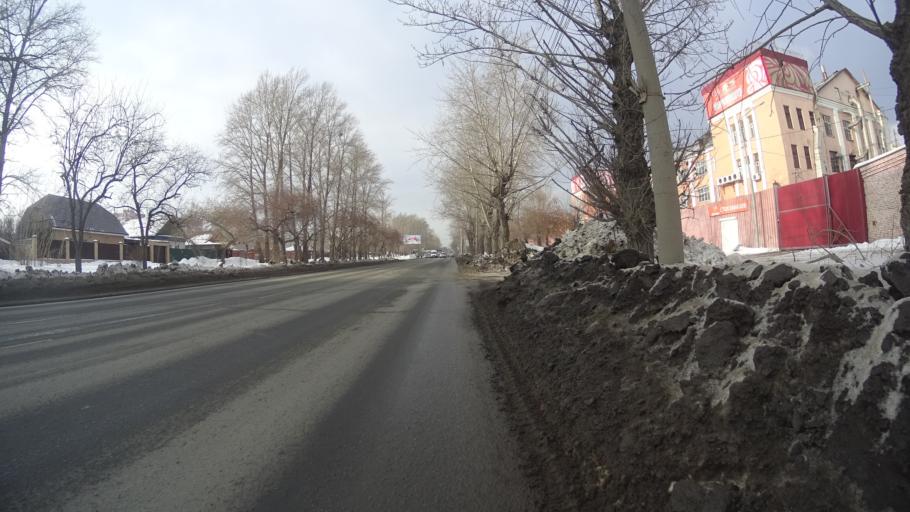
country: RU
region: Chelyabinsk
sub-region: Gorod Chelyabinsk
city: Chelyabinsk
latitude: 55.1229
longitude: 61.3750
